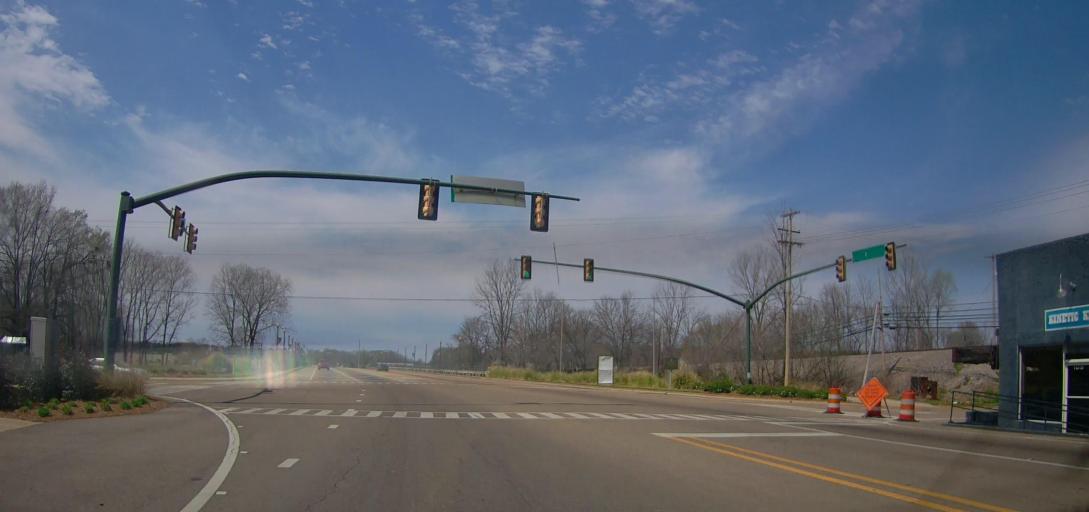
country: US
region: Mississippi
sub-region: Union County
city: New Albany
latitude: 34.4948
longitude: -89.0107
